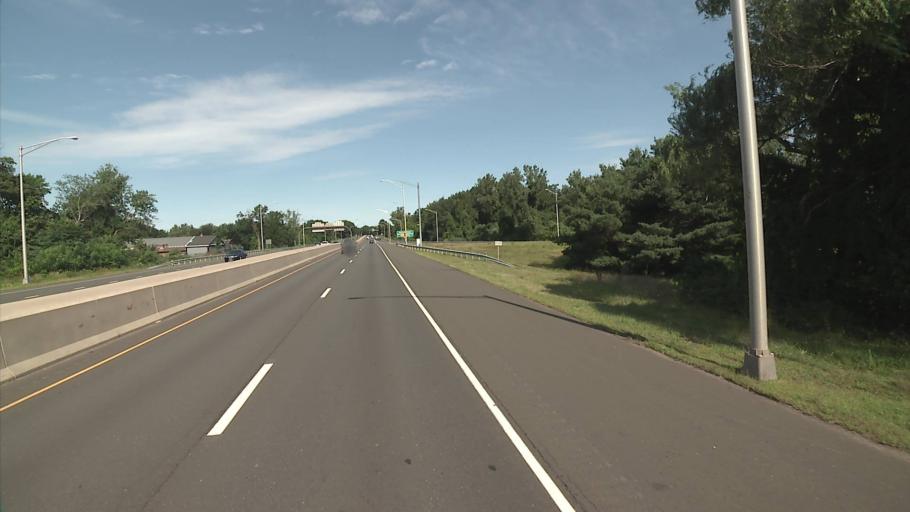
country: US
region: Connecticut
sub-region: Hartford County
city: Glastonbury
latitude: 41.7297
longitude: -72.6165
